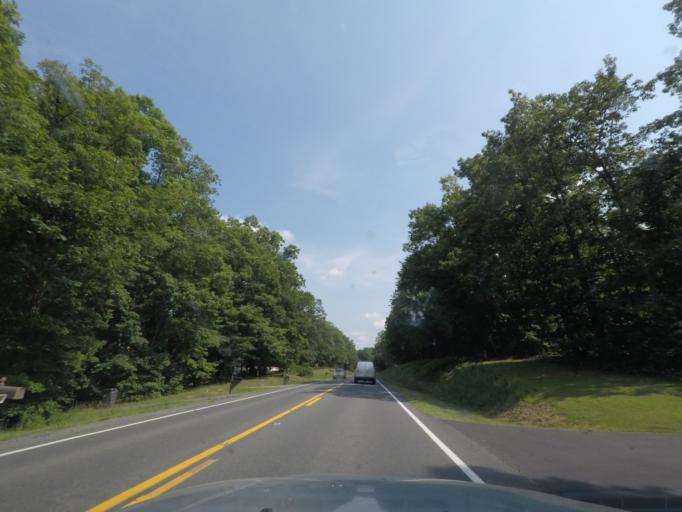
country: US
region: Virginia
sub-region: Fluvanna County
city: Palmyra
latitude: 37.8271
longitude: -78.2714
